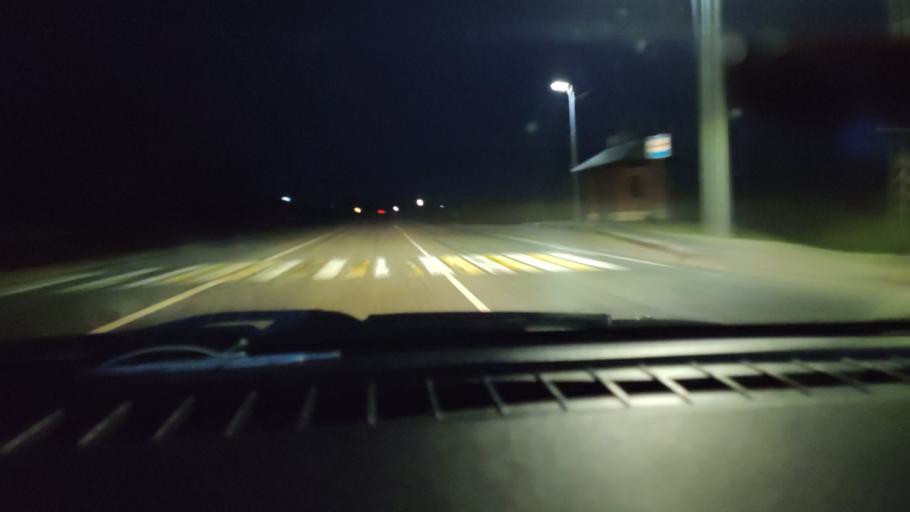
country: RU
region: Udmurtiya
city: Pychas
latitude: 56.4882
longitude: 52.5721
